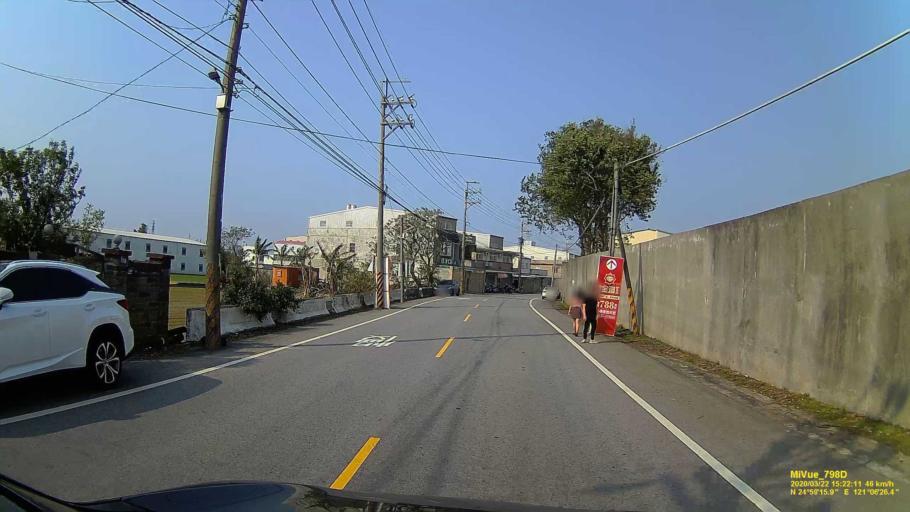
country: TW
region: Taiwan
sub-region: Hsinchu
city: Zhubei
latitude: 24.9879
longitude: 121.1074
